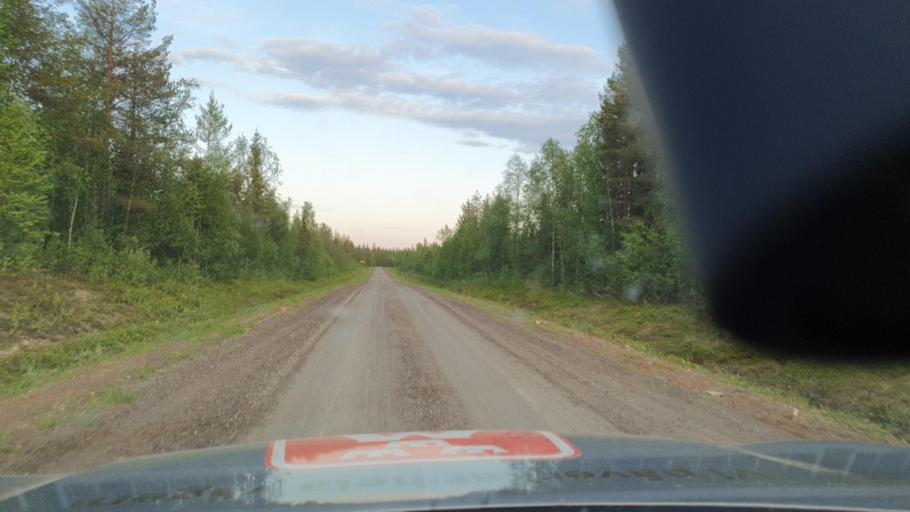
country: SE
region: Norrbotten
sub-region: Bodens Kommun
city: Boden
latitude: 66.5087
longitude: 21.5368
